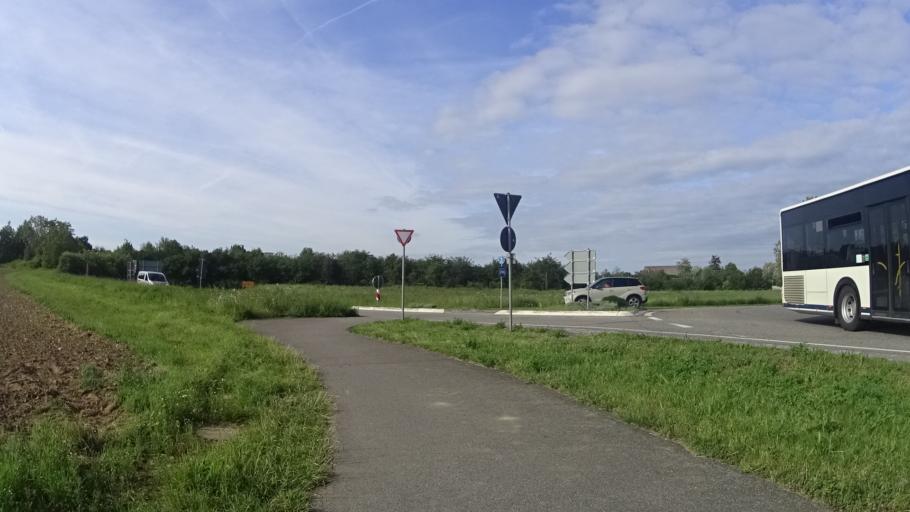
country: DE
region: Baden-Wuerttemberg
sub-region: Freiburg Region
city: Neuenburg am Rhein
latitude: 47.8213
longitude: 7.5704
